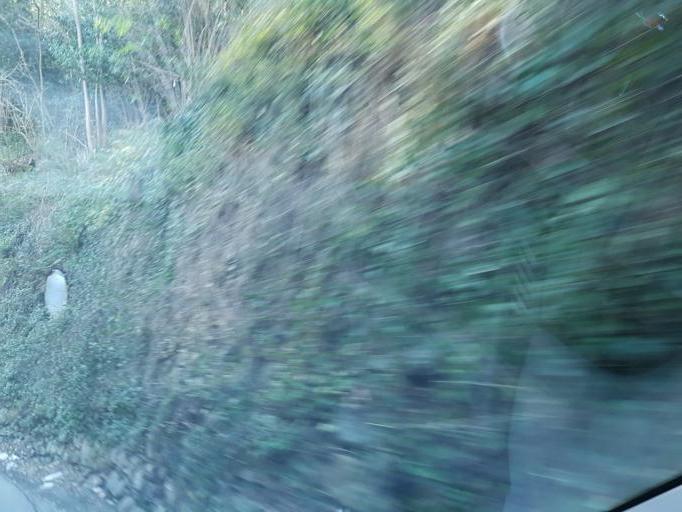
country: IT
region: Liguria
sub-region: Provincia di Genova
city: Campomorone
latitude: 44.5085
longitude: 8.8840
